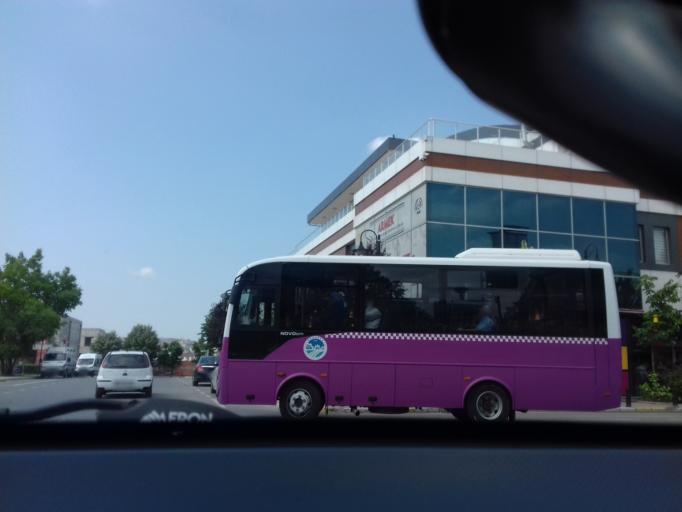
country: TR
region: Sakarya
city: Adapazari
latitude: 40.7145
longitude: 30.3610
